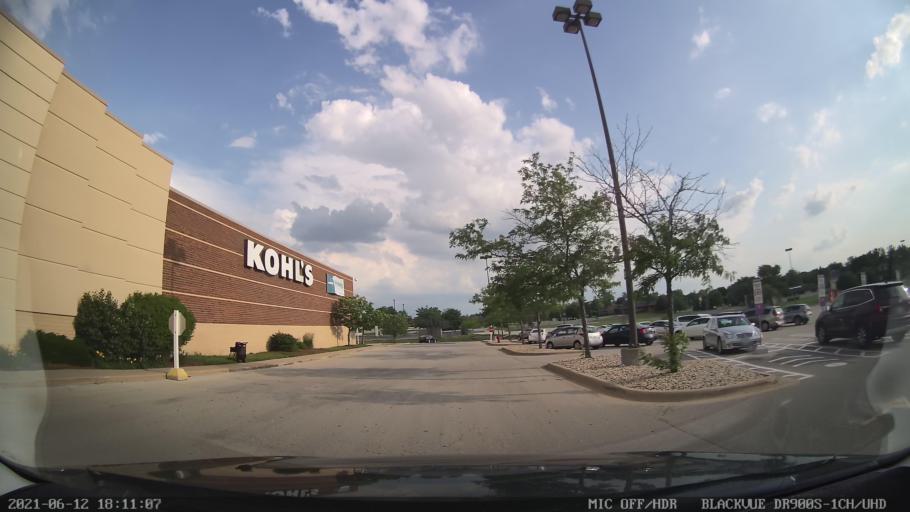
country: US
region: Illinois
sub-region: McLean County
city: Bloomington
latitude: 40.4853
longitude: -88.9586
